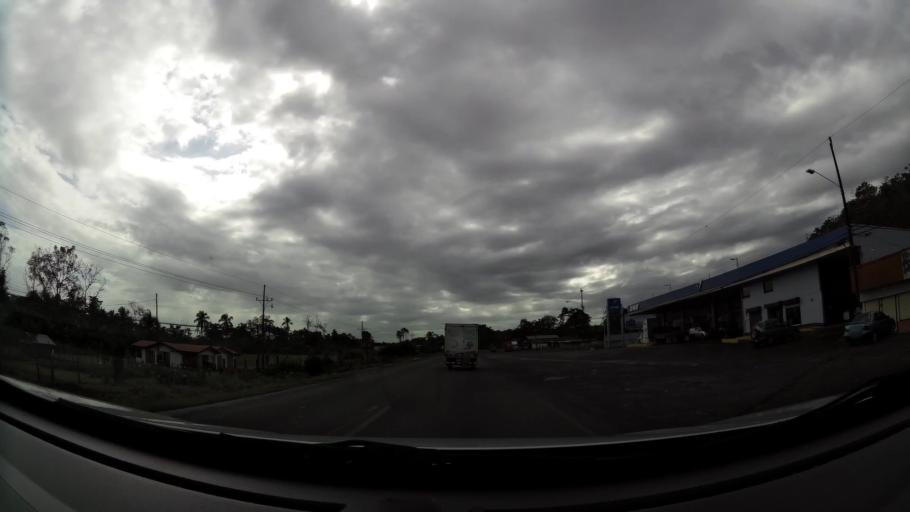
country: CR
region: Limon
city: Pocora
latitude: 10.1678
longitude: -83.6055
